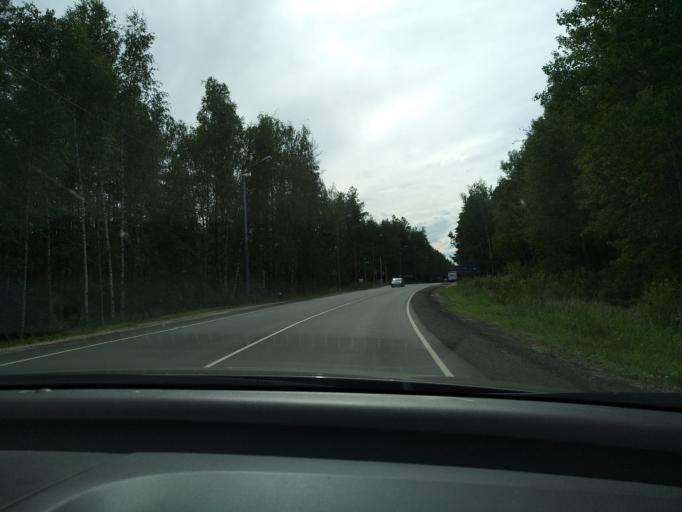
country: RU
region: Moskovskaya
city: Krasnyy Tkach
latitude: 55.3994
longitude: 39.1293
